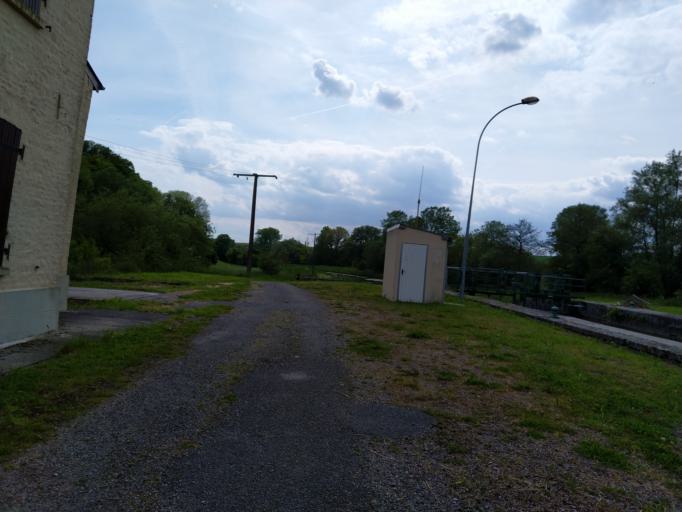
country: FR
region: Picardie
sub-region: Departement de l'Aisne
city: Guise
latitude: 49.9513
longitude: 3.5994
